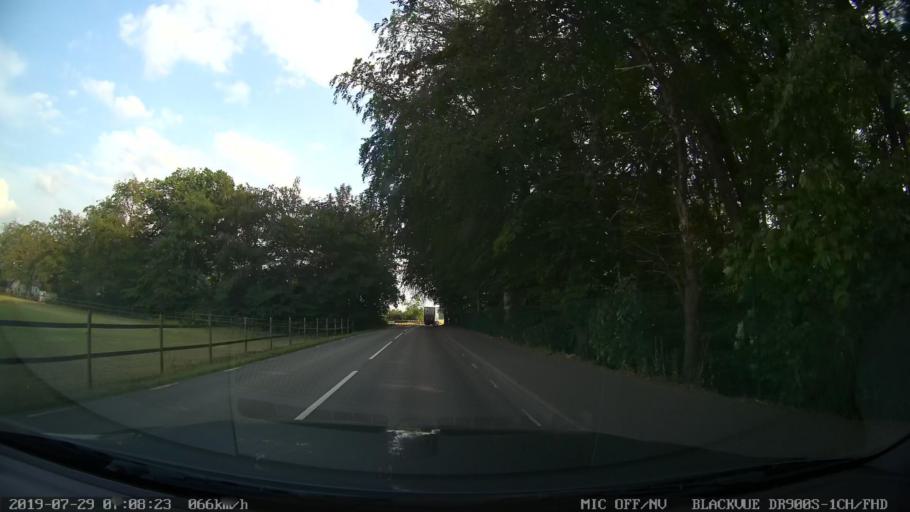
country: SE
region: Skane
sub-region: Helsingborg
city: Odakra
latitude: 56.0994
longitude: 12.6985
